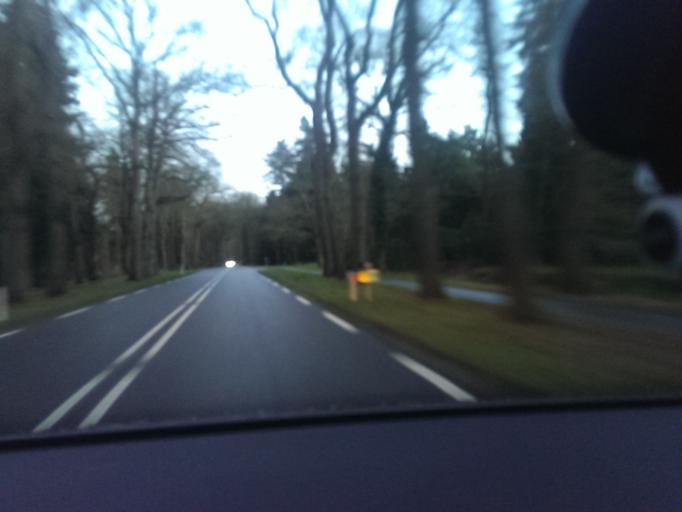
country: NL
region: Overijssel
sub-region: Gemeente Twenterand
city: Den Ham
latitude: 52.4895
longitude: 6.4480
